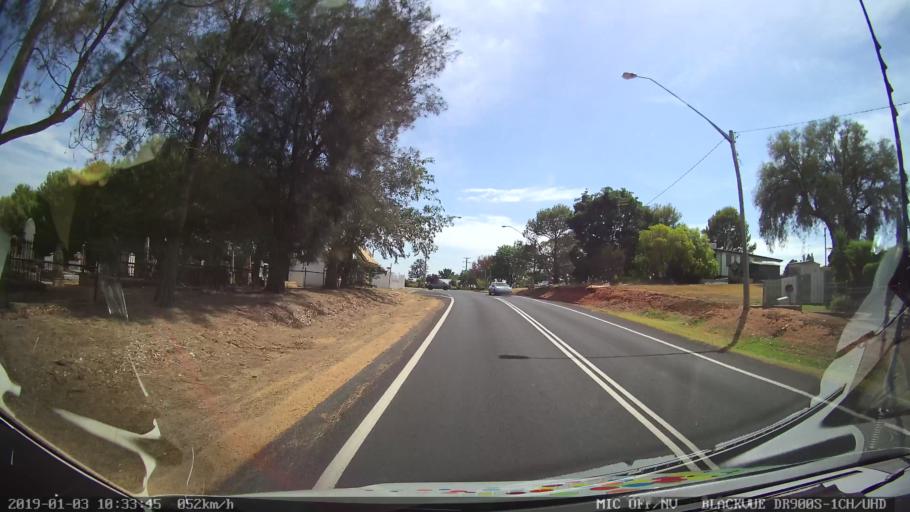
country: AU
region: New South Wales
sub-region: Young
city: Young
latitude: -34.3261
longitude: 148.2896
